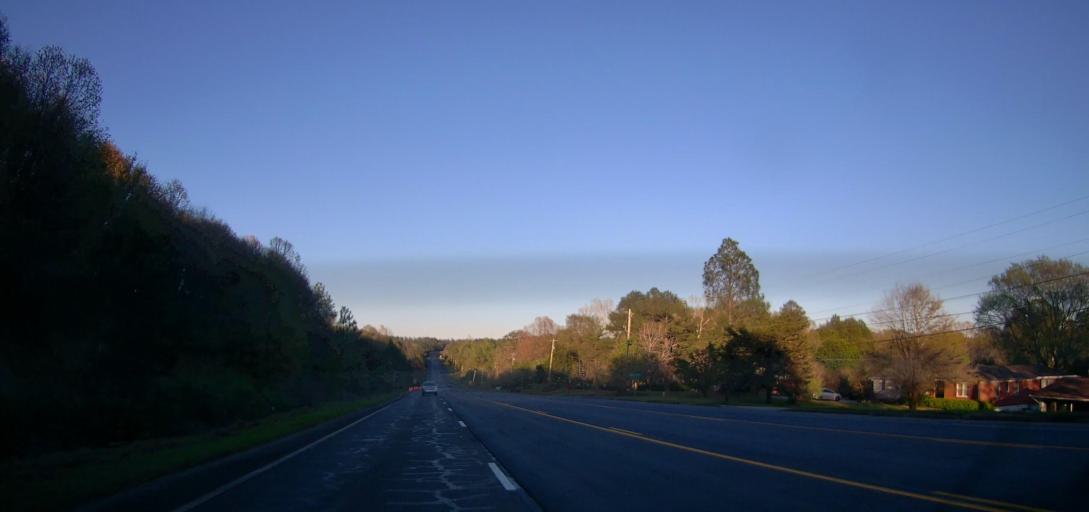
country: US
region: Georgia
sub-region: Bibb County
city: Macon
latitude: 32.8446
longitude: -83.5425
